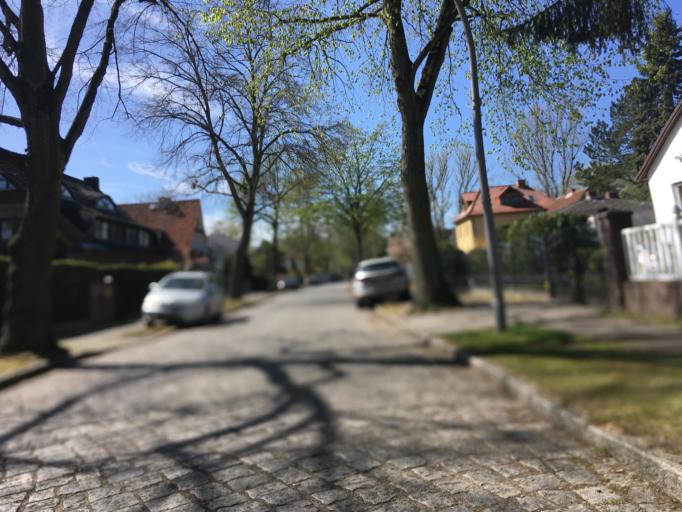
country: DE
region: Berlin
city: Hermsdorf
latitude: 52.6074
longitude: 13.2982
